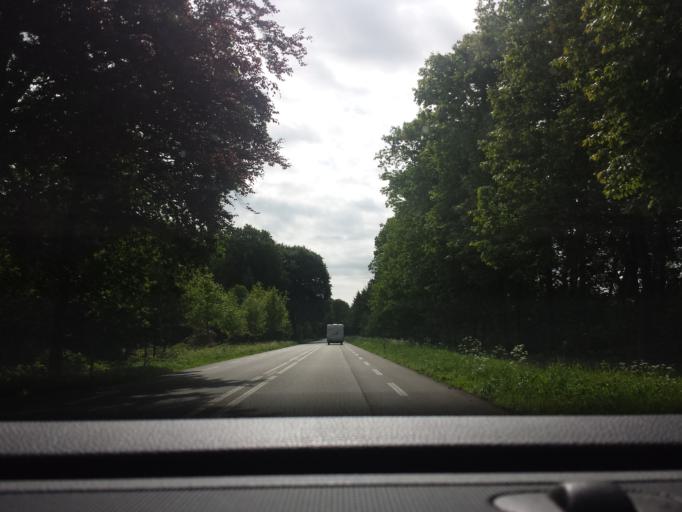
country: NL
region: Gelderland
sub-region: Gemeente Lochem
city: Barchem
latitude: 52.0934
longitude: 6.4007
